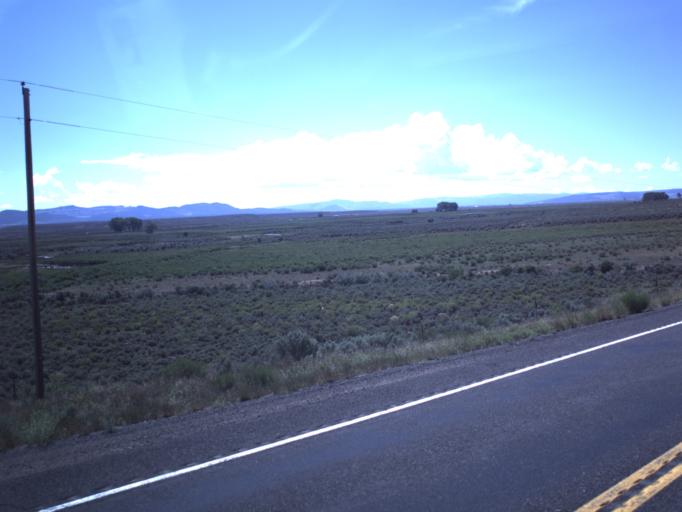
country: US
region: Utah
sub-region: Garfield County
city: Panguitch
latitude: 37.9620
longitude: -112.4138
